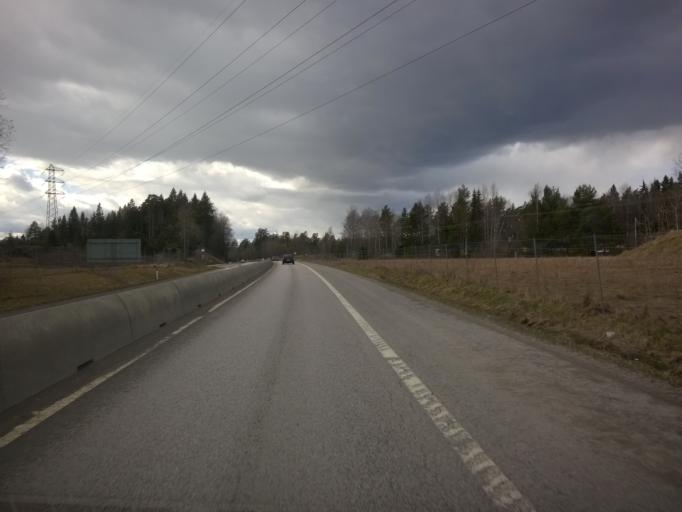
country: SE
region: Stockholm
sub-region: Jarfalla Kommun
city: Jakobsberg
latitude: 59.4773
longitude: 17.8483
